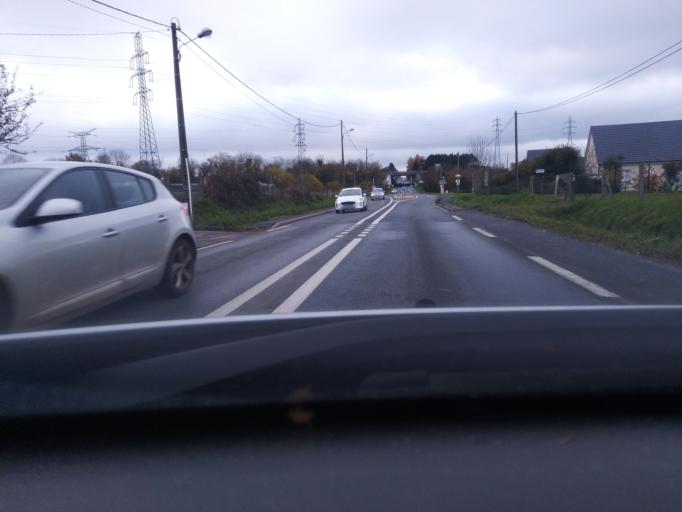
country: FR
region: Haute-Normandie
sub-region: Departement de la Seine-Maritime
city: La Vaupaliere
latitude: 49.4926
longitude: 0.9956
